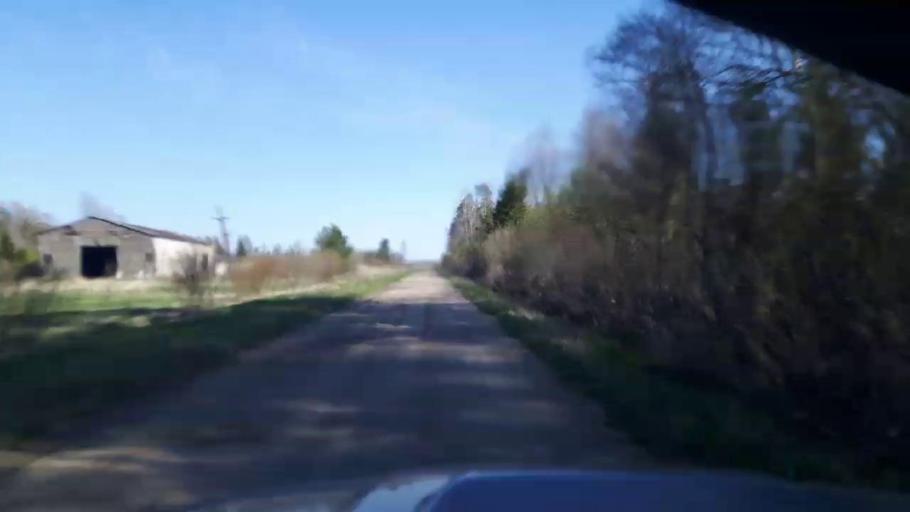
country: EE
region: Paernumaa
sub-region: Vaendra vald (alev)
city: Vandra
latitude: 58.5176
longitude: 24.9606
